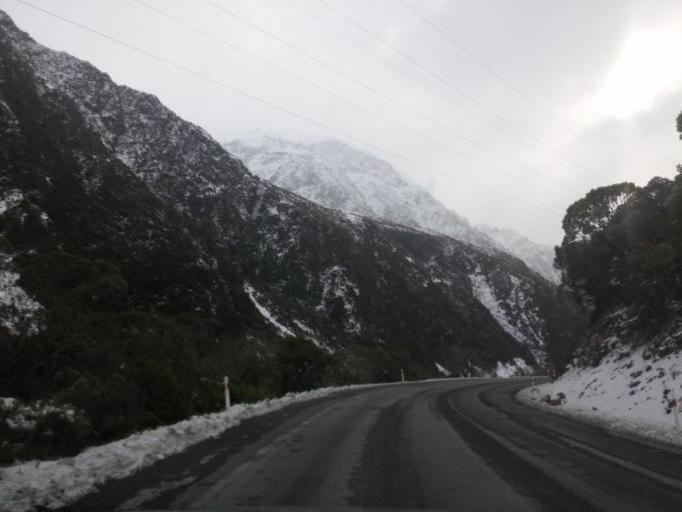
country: NZ
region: West Coast
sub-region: Grey District
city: Greymouth
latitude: -42.8936
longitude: 171.5584
